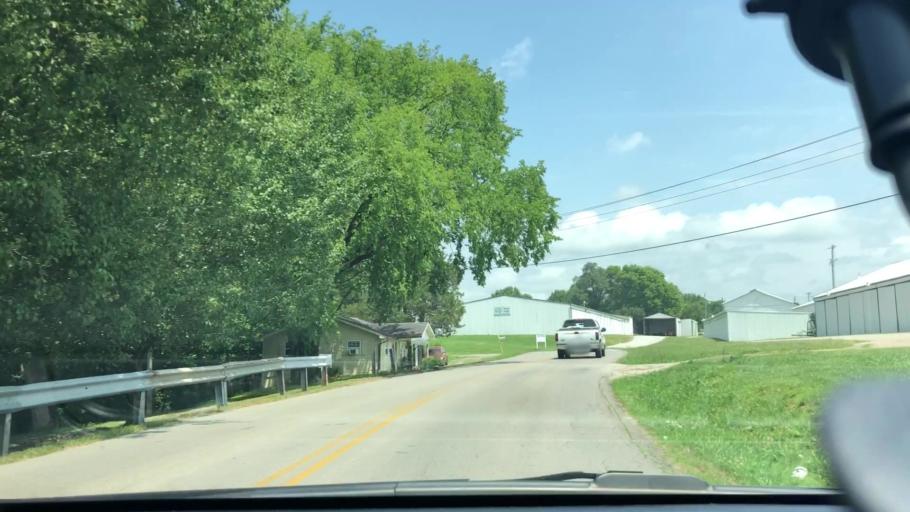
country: US
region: Kentucky
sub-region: Pulaski County
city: Somerset
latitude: 37.0614
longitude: -84.6734
